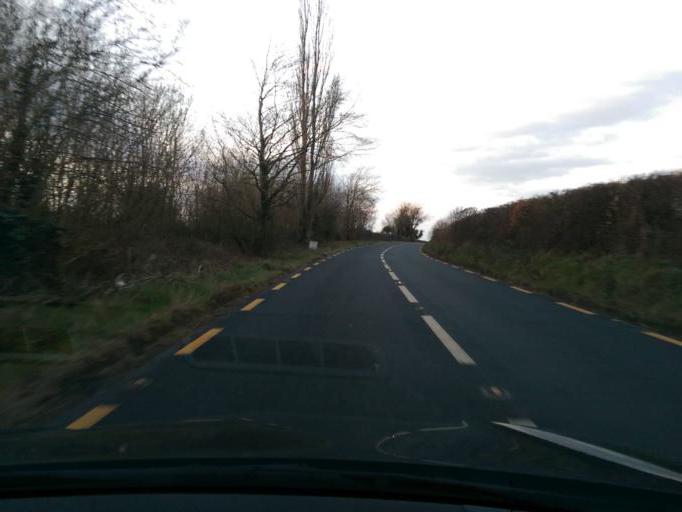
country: IE
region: Munster
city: Nenagh Bridge
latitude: 52.9694
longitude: -8.1352
